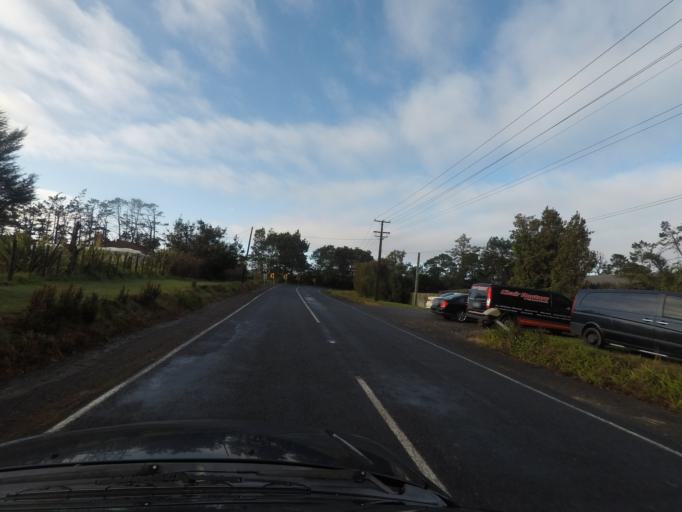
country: NZ
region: Auckland
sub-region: Auckland
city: Waitakere
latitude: -36.9091
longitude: 174.6089
